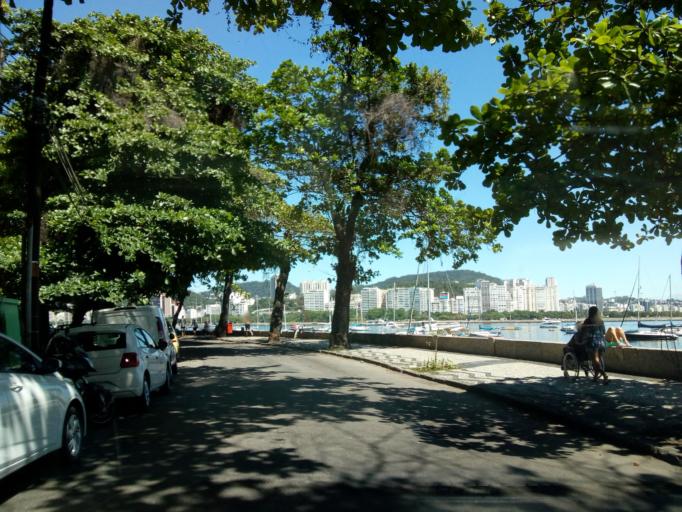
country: BR
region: Rio de Janeiro
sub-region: Rio De Janeiro
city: Rio de Janeiro
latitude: -22.9480
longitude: -43.1642
